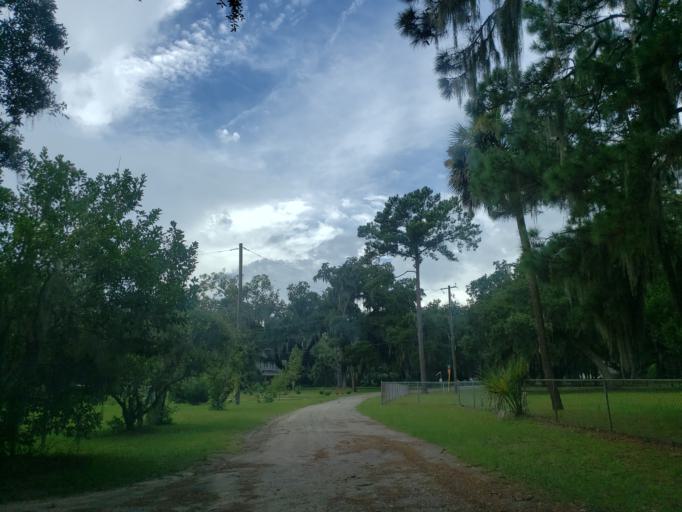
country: US
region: Georgia
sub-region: Chatham County
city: Wilmington Island
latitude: 31.9752
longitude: -80.9972
